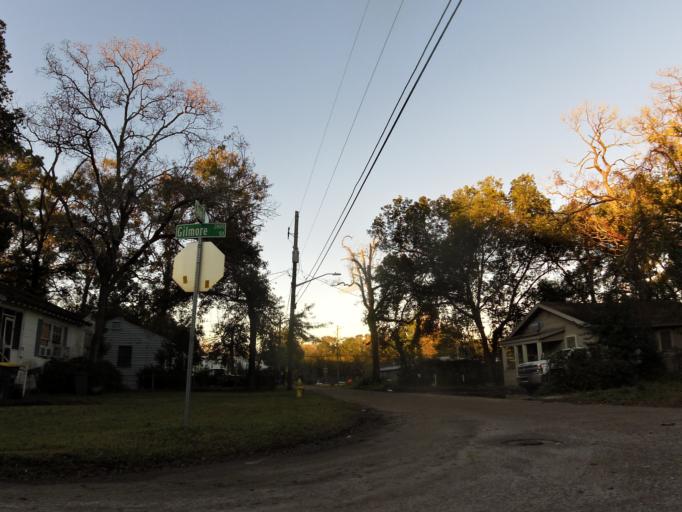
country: US
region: Florida
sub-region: Duval County
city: Jacksonville
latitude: 30.3183
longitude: -81.6991
